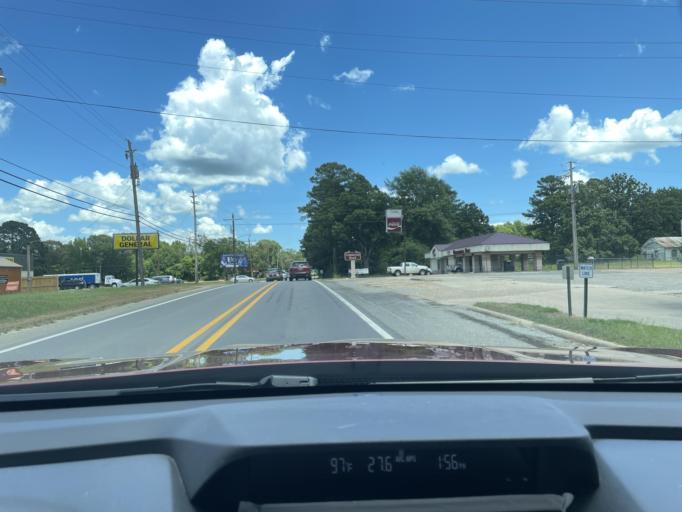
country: US
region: Arkansas
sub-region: Drew County
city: Monticello
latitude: 33.6288
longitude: -91.7782
